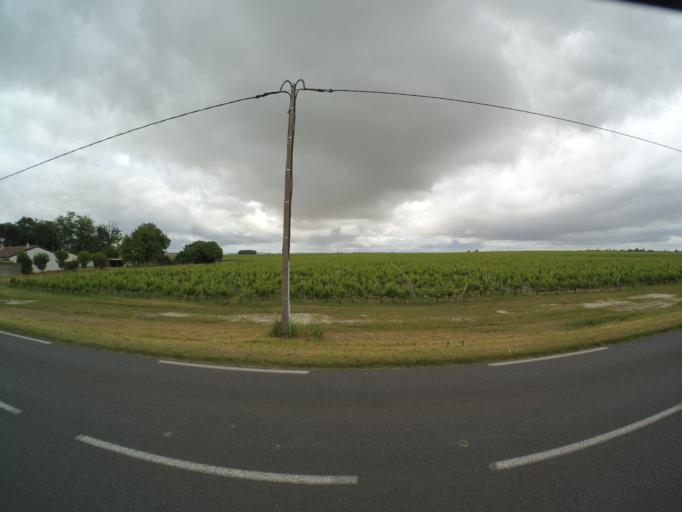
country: FR
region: Aquitaine
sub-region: Departement de la Gironde
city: Lamarque
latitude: 45.0842
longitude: -0.7268
